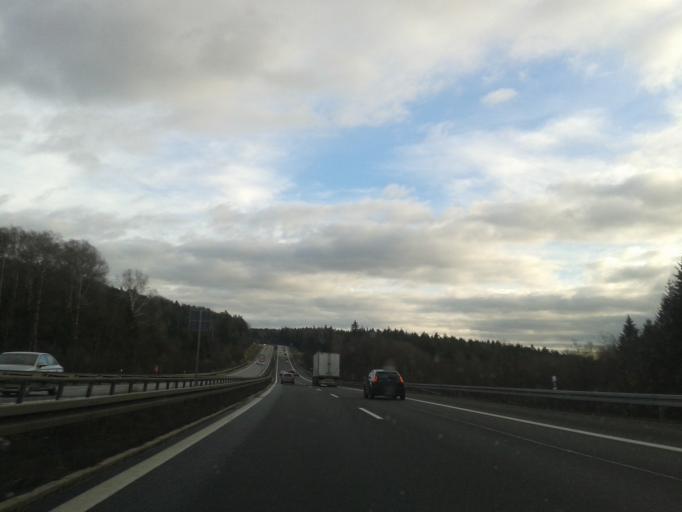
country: DE
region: Saxony
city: Rammenau
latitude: 51.1740
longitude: 14.1115
